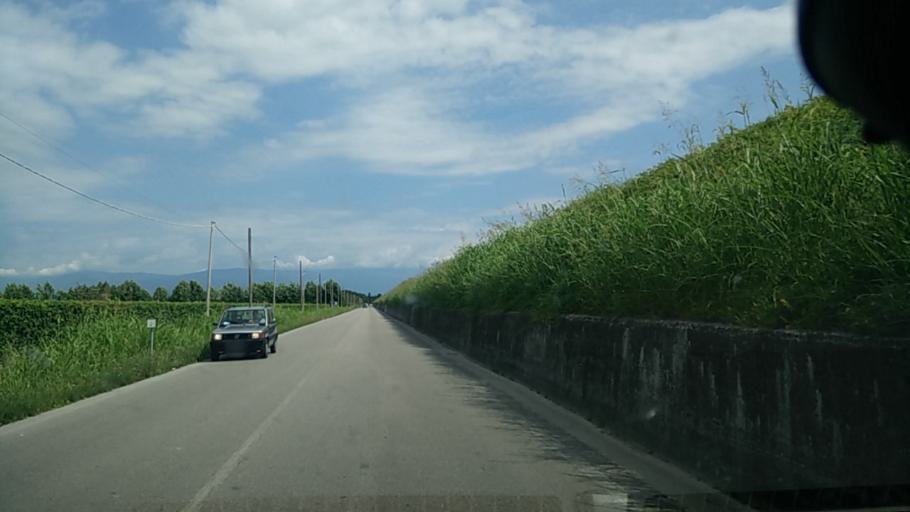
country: IT
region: Friuli Venezia Giulia
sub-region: Provincia di Pordenone
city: Puia-Villanova
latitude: 45.8297
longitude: 12.5697
